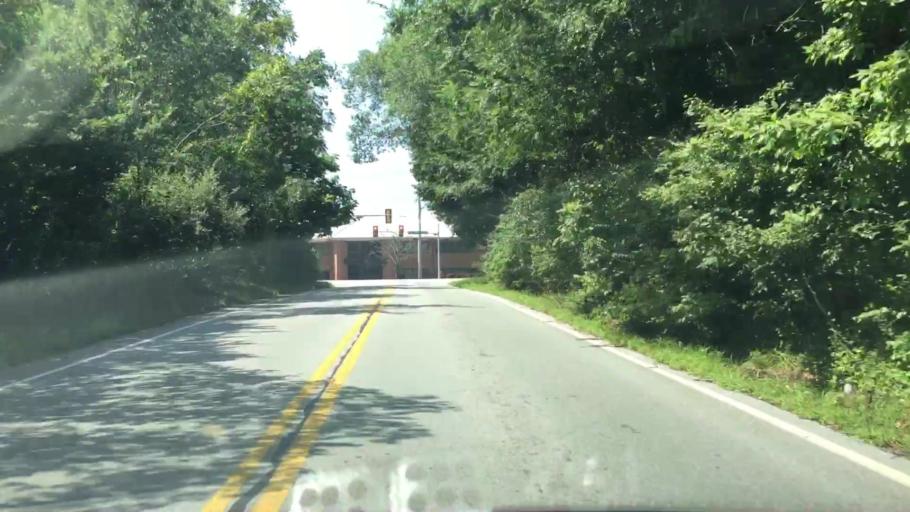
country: US
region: Pennsylvania
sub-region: Delaware County
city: Lima
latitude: 39.9062
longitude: -75.4149
